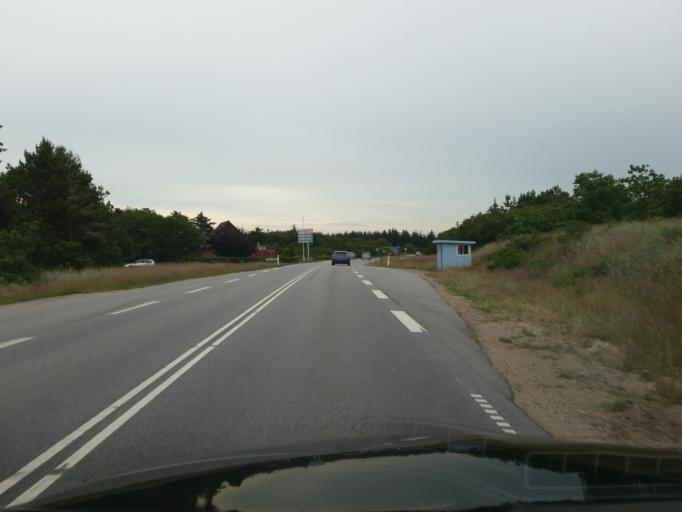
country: DK
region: South Denmark
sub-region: Varde Kommune
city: Oksbol
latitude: 55.8149
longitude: 8.2103
